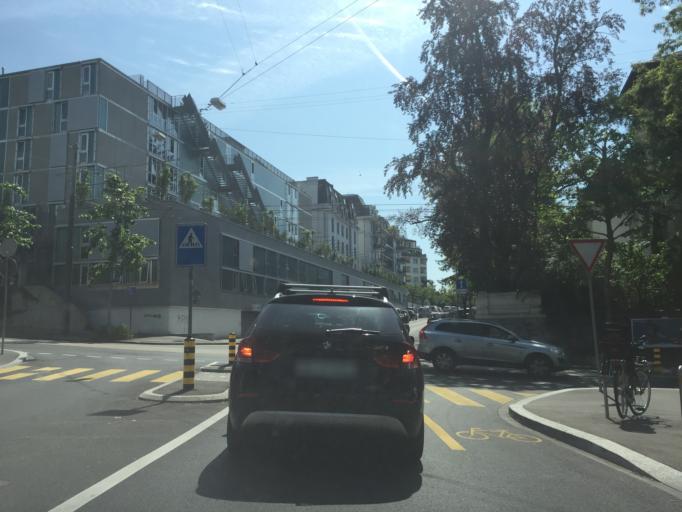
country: CH
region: Vaud
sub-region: Lausanne District
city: Lausanne
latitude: 46.5138
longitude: 6.6306
